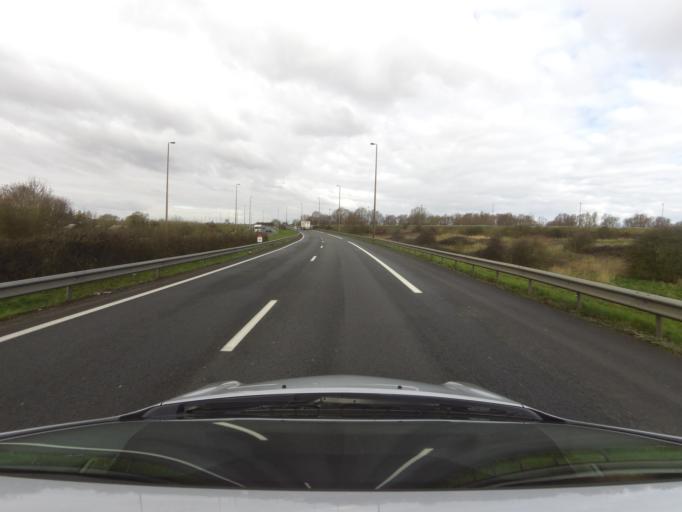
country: FR
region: Nord-Pas-de-Calais
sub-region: Departement du Pas-de-Calais
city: Coulogne
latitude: 50.9357
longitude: 1.8785
